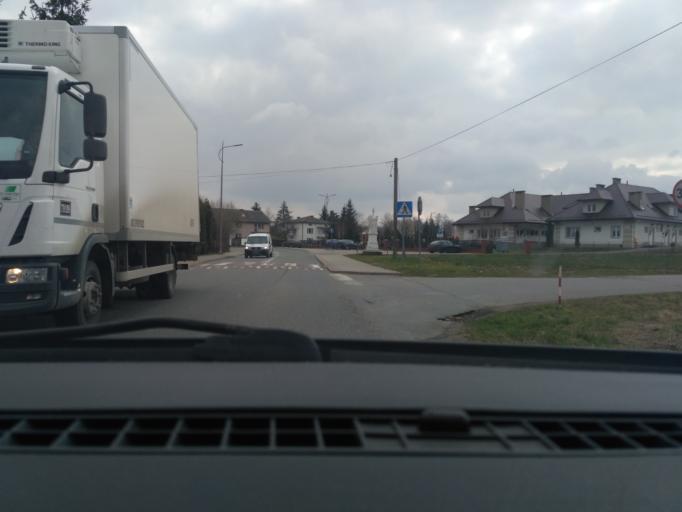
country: PL
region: Subcarpathian Voivodeship
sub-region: Powiat krosnienski
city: Kroscienko Wyzne
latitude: 49.6740
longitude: 21.8276
